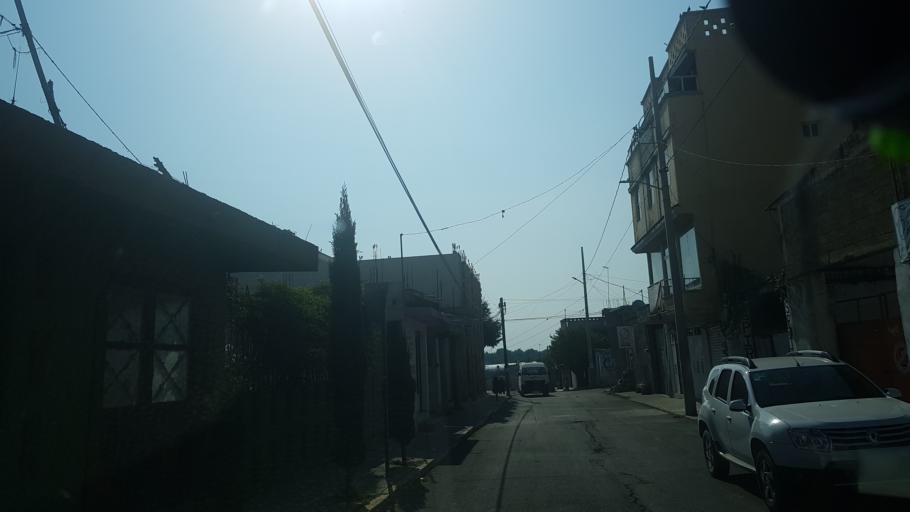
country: MX
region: Puebla
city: San Nicolas de los Ranchos
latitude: 19.0730
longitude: -98.4843
